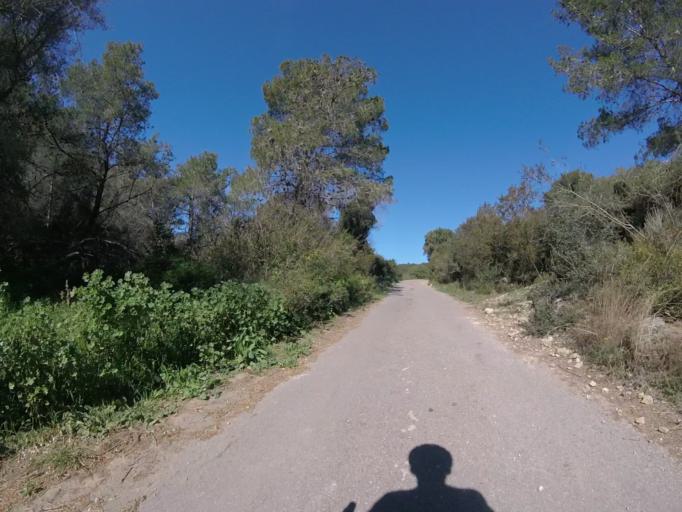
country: ES
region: Valencia
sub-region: Provincia de Castello
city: Benicassim
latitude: 40.0813
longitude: 0.0877
